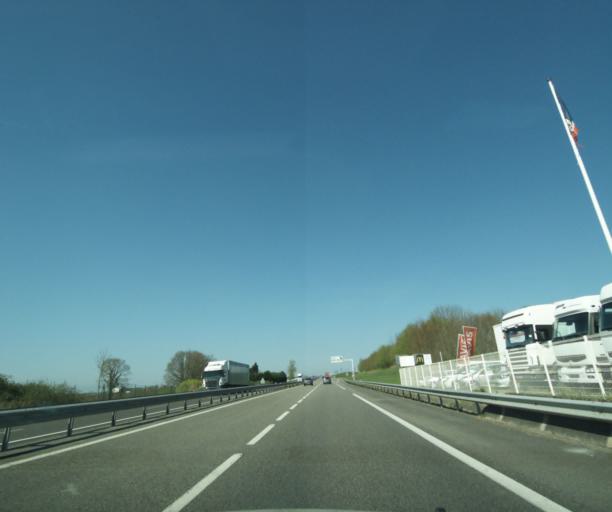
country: FR
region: Bourgogne
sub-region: Departement de la Nievre
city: Cosne-Cours-sur-Loire
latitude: 47.3787
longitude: 2.9232
